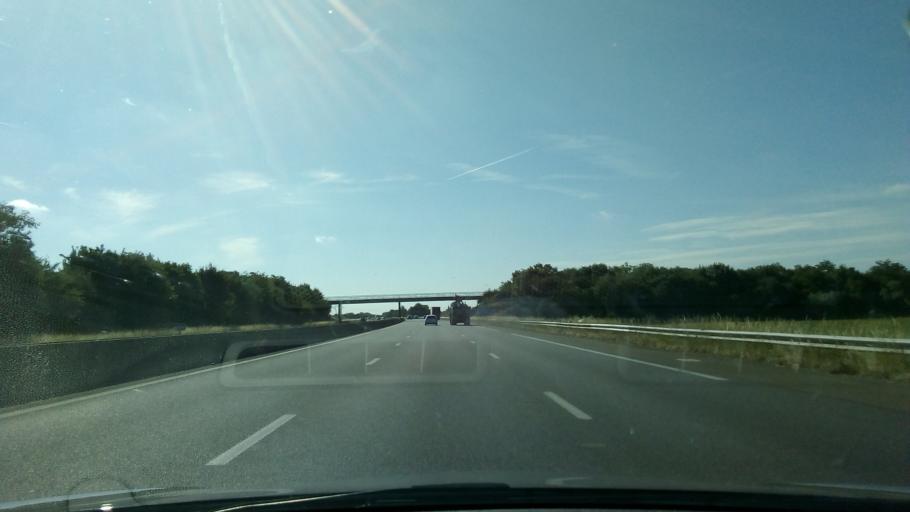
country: FR
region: Ile-de-France
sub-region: Departement de Seine-et-Marne
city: Moissy-Cramayel
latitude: 48.6061
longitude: 2.5853
